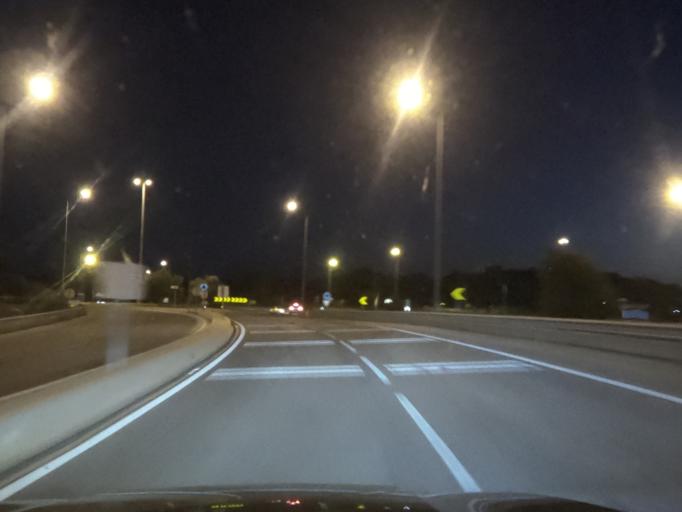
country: PT
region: Faro
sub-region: Loule
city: Loule
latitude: 37.1451
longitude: -8.0417
